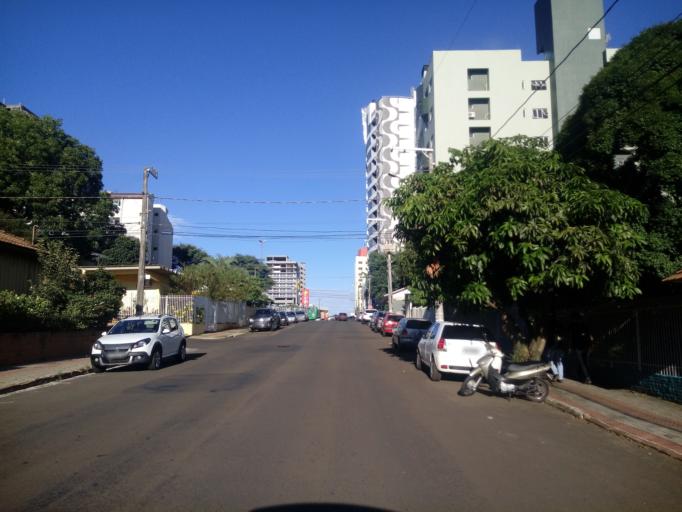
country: BR
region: Santa Catarina
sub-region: Chapeco
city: Chapeco
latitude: -27.0934
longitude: -52.6142
